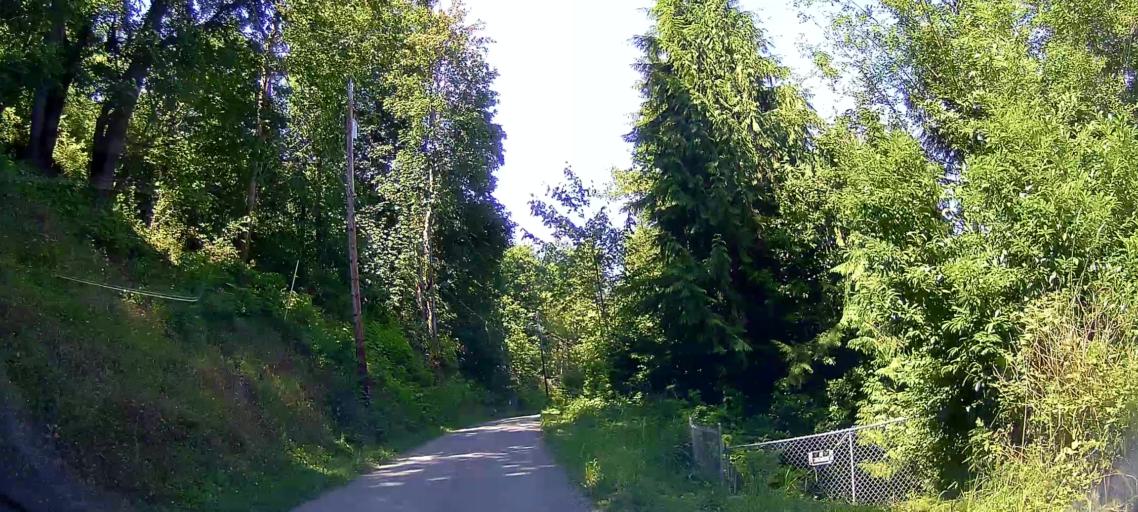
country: US
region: Washington
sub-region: Whatcom County
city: Sudden Valley
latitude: 48.6504
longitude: -122.3334
